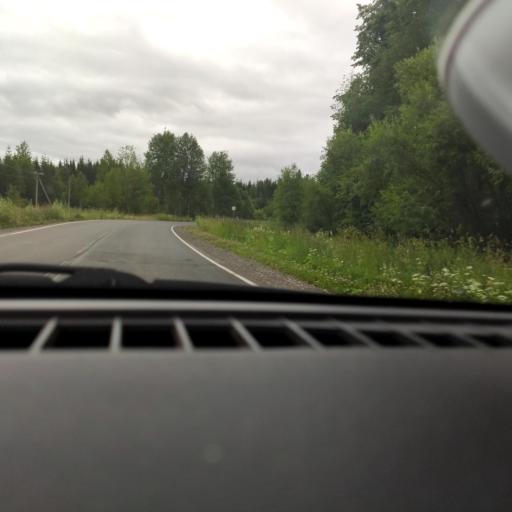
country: RU
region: Perm
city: Polazna
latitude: 58.3383
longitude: 56.1722
